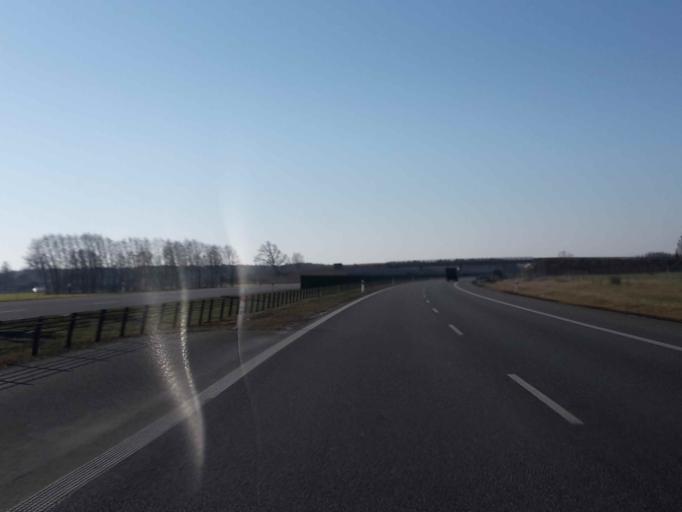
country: PL
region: Kujawsko-Pomorskie
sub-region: Powiat torunski
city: Lubicz Dolny
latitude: 52.9904
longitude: 18.7352
